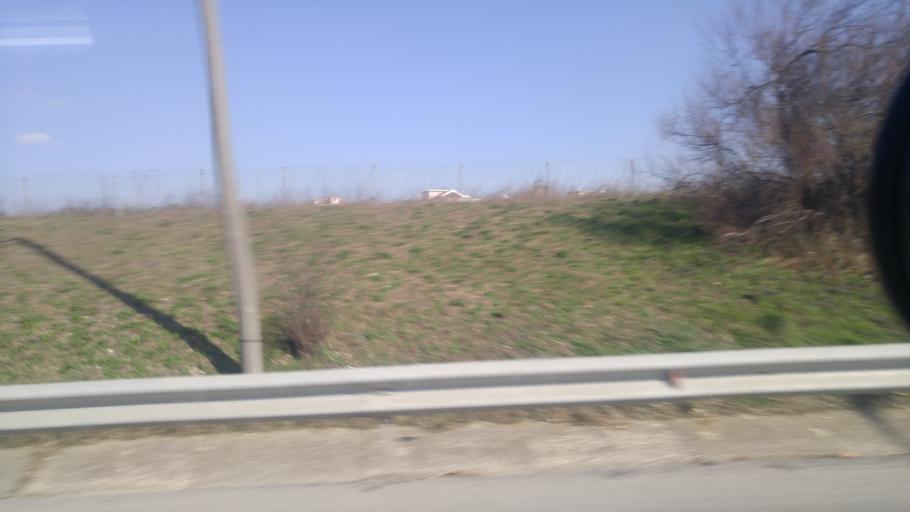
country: TR
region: Istanbul
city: Ortakoy
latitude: 41.0786
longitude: 28.3733
